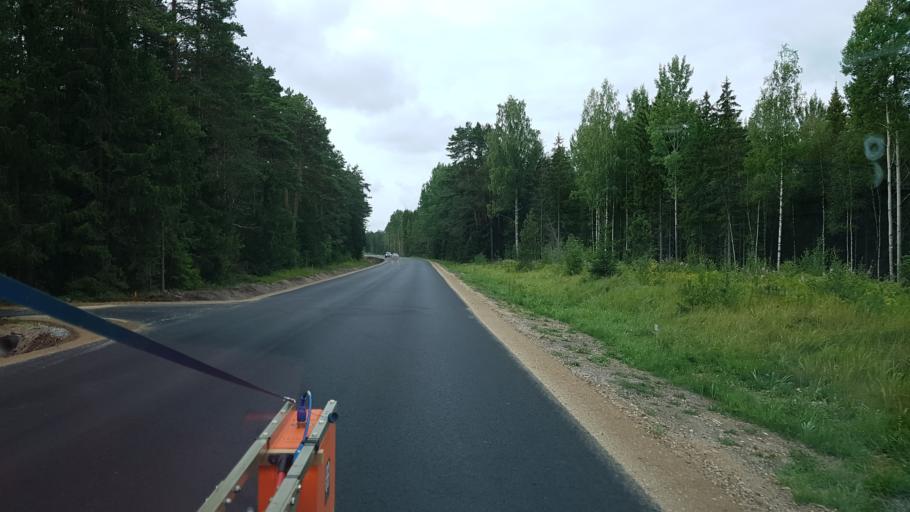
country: EE
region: Harju
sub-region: Nissi vald
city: Turba
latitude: 59.1228
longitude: 24.0632
